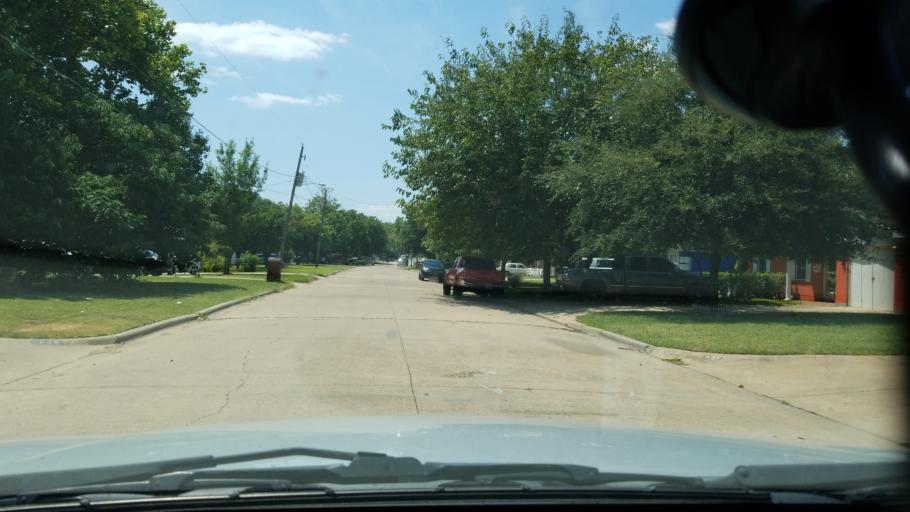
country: US
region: Texas
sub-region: Dallas County
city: Grand Prairie
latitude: 32.7596
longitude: -96.9569
